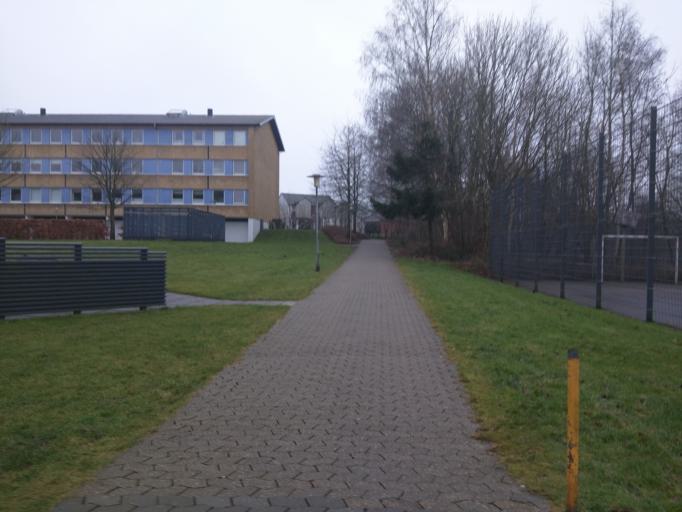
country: DK
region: South Denmark
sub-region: Fredericia Kommune
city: Snoghoj
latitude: 55.5478
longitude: 9.7108
